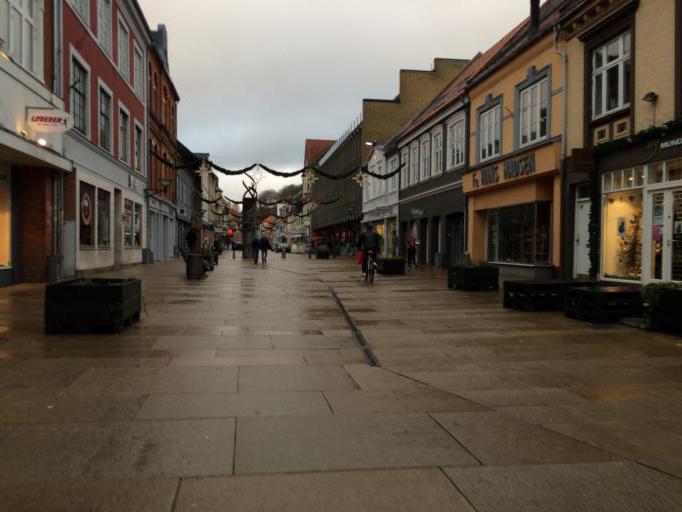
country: DK
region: South Denmark
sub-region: Vejle Kommune
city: Vejle
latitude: 55.7123
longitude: 9.5365
